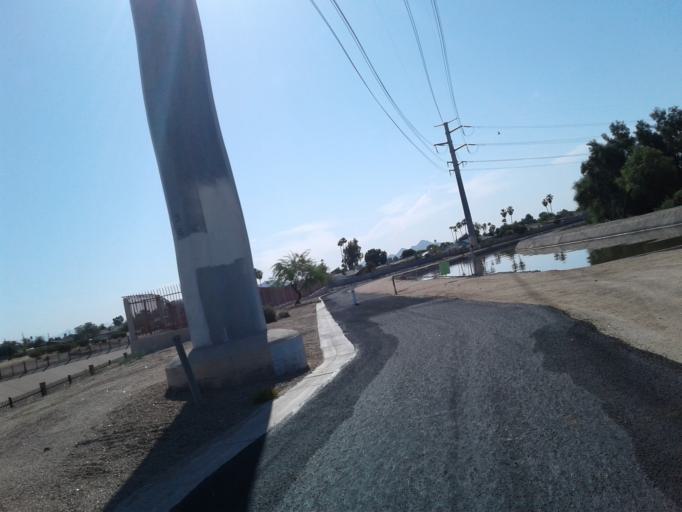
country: US
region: Arizona
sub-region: Maricopa County
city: Glendale
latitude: 33.5955
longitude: -112.1685
